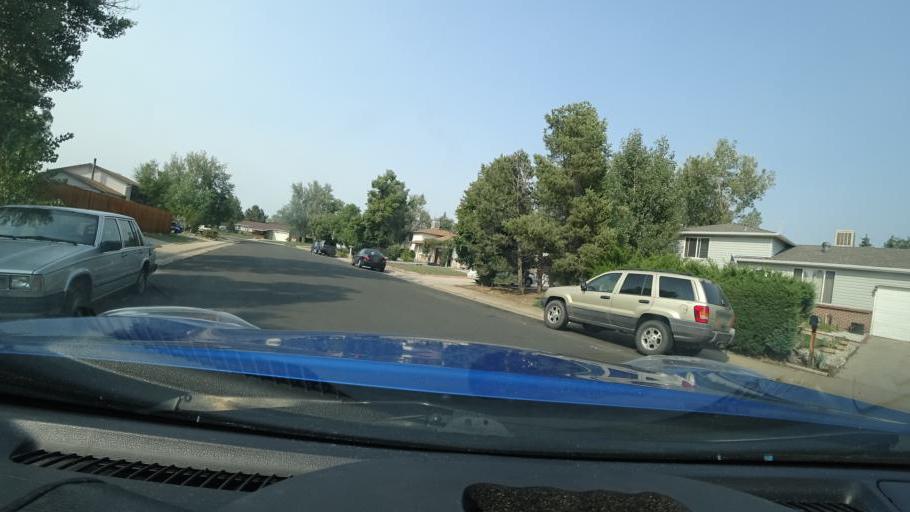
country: US
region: Colorado
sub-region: Adams County
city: Aurora
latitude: 39.6653
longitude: -104.8067
